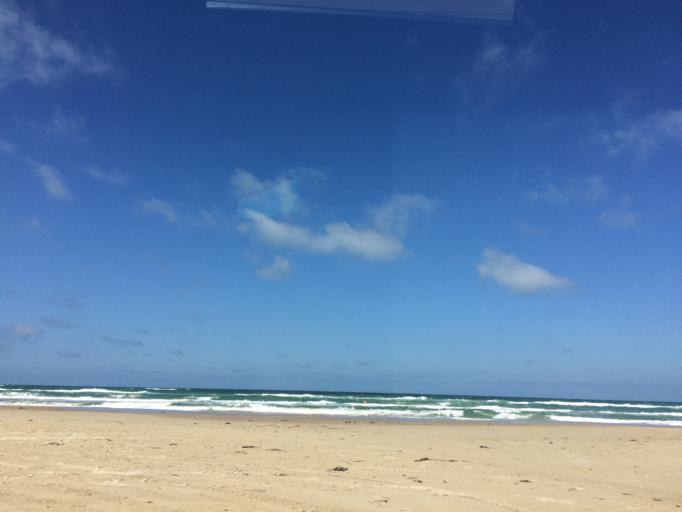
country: DK
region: North Denmark
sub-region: Jammerbugt Kommune
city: Brovst
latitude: 57.2248
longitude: 9.5386
